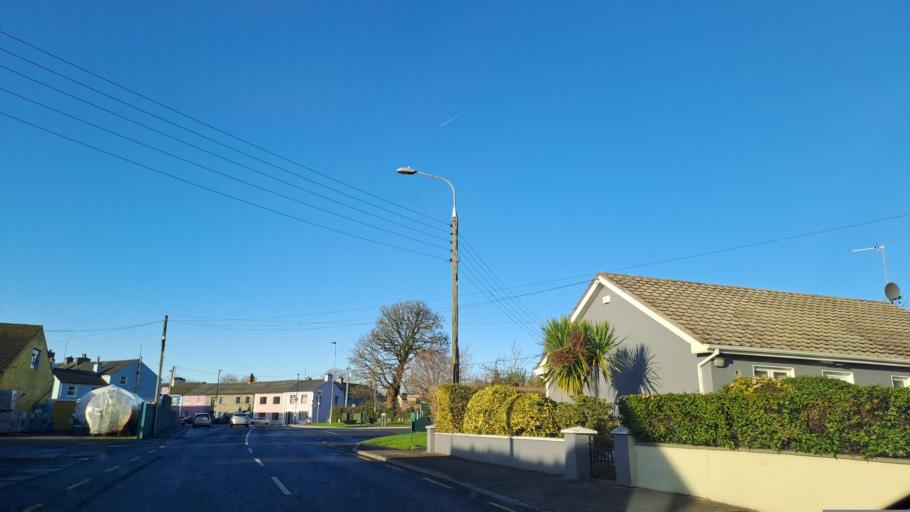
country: IE
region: Ulster
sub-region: An Cabhan
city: Mullagh
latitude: 53.8109
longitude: -6.9431
